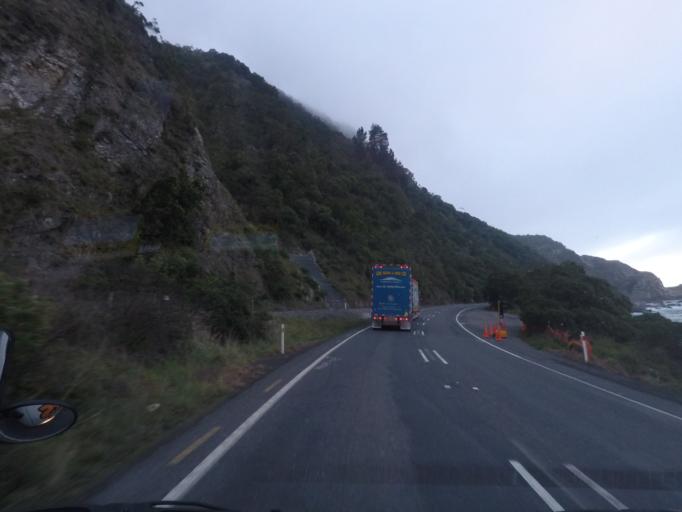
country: NZ
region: Canterbury
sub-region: Kaikoura District
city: Kaikoura
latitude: -42.4510
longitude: 173.5690
